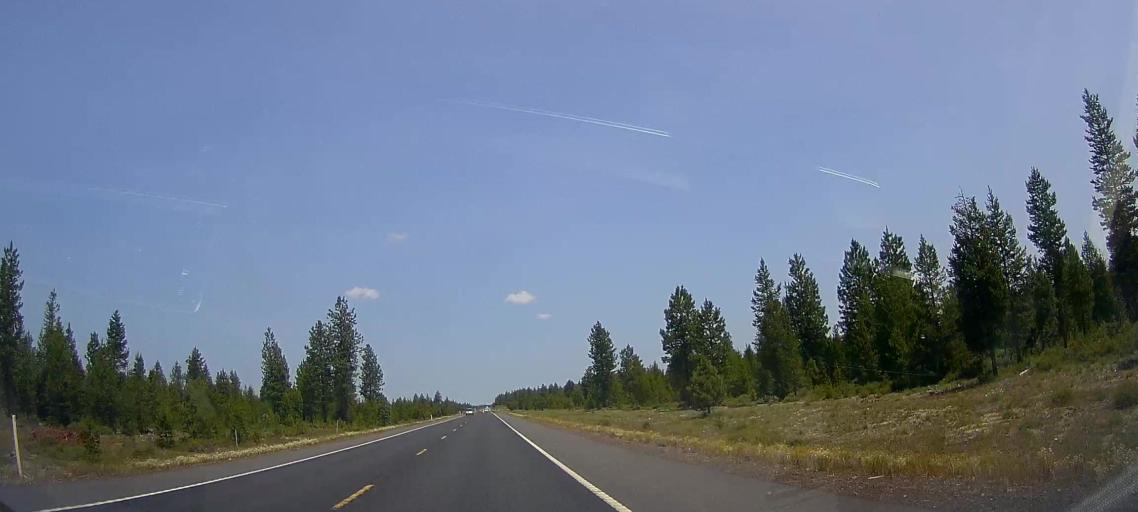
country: US
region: Oregon
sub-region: Deschutes County
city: La Pine
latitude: 43.5024
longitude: -121.6667
